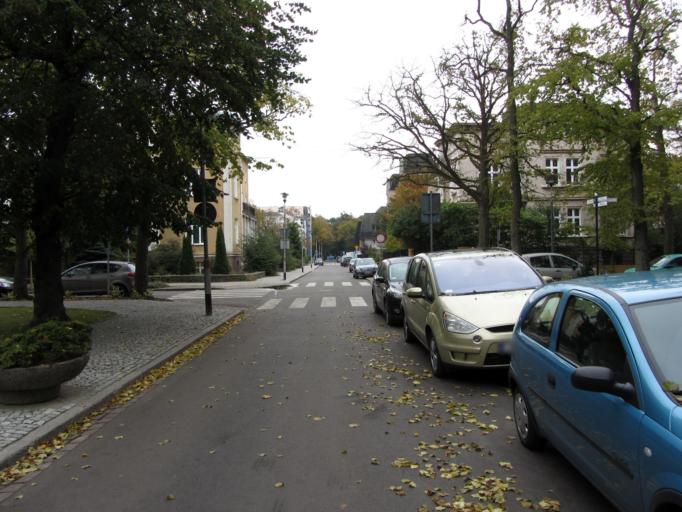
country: PL
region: West Pomeranian Voivodeship
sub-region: Powiat kolobrzeski
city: Kolobrzeg
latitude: 54.1836
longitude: 15.5722
